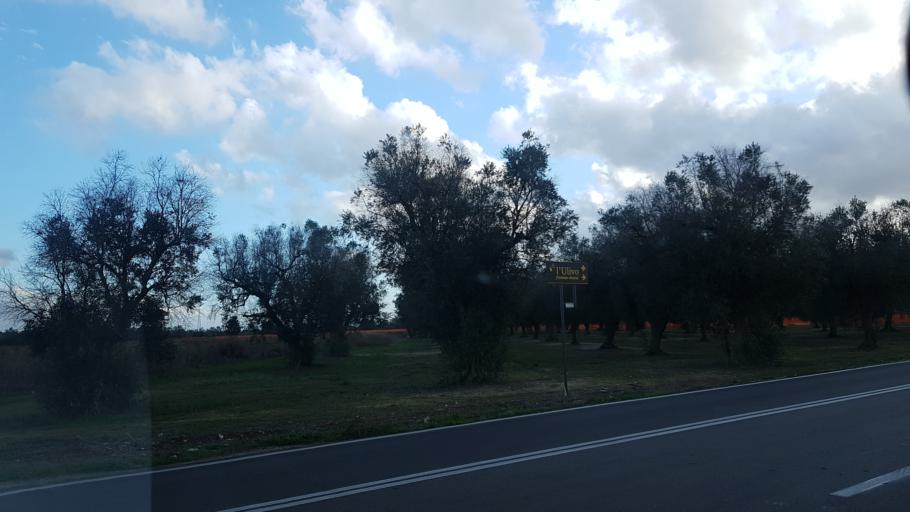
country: IT
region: Apulia
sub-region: Provincia di Brindisi
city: San Pietro Vernotico
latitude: 40.5195
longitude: 18.0145
